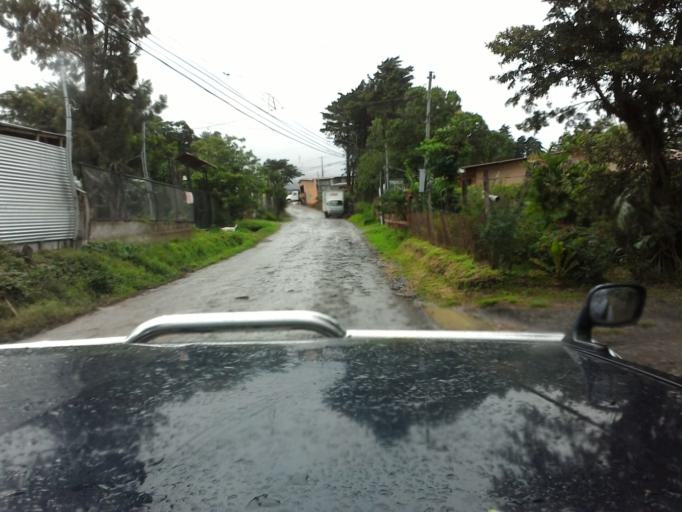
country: CR
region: Guanacaste
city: Juntas
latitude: 10.3153
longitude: -84.8281
